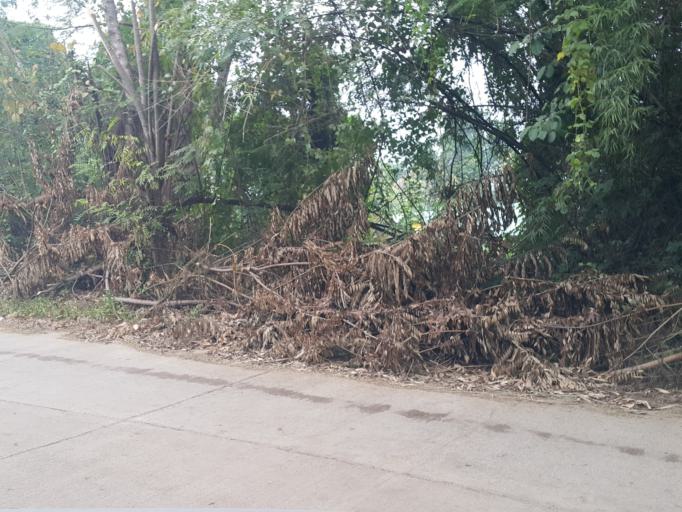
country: TH
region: Chiang Mai
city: Pai
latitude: 19.3602
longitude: 98.4489
